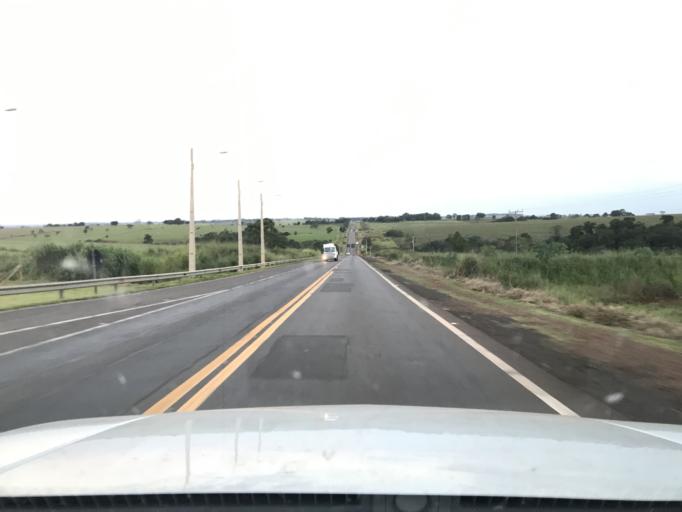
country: BR
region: Mato Grosso do Sul
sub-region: Eldorado
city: Eldorado
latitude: -23.8695
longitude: -54.3268
